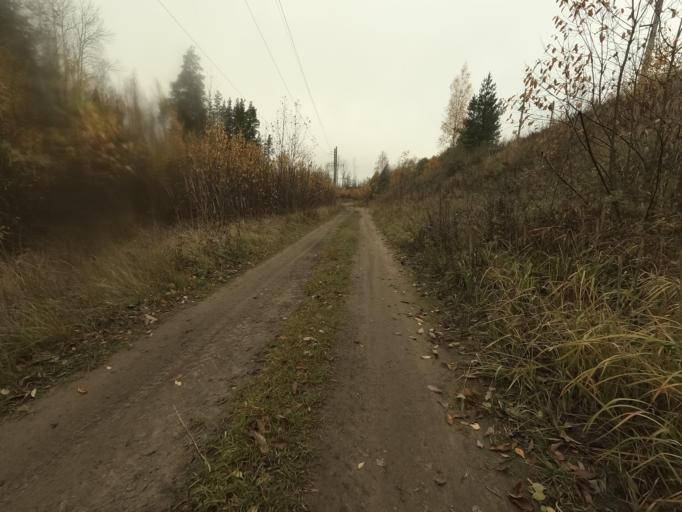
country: RU
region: Leningrad
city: Pavlovo
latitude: 59.7703
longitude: 30.9080
